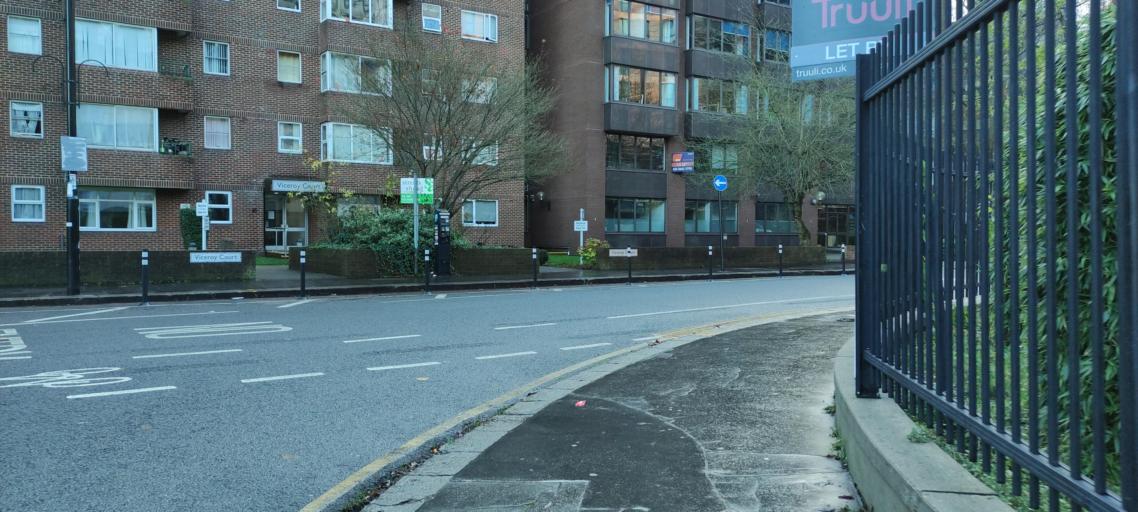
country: GB
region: England
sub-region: Greater London
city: Croydon
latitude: 51.3784
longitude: -0.0957
